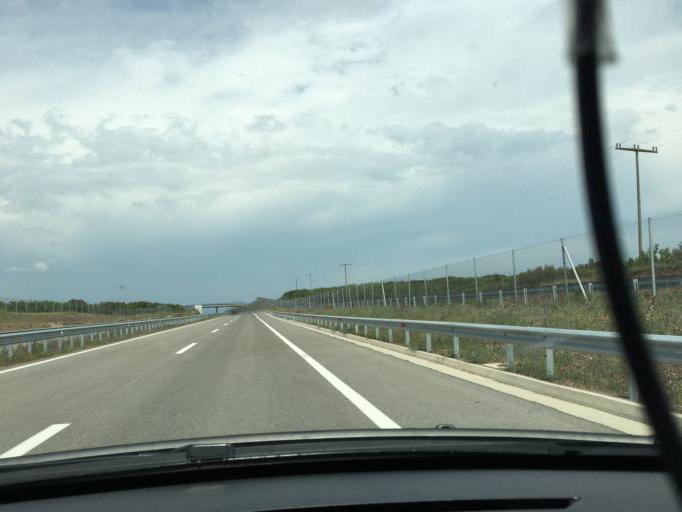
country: MK
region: Gevgelija
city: Miravci
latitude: 41.2681
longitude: 22.4685
